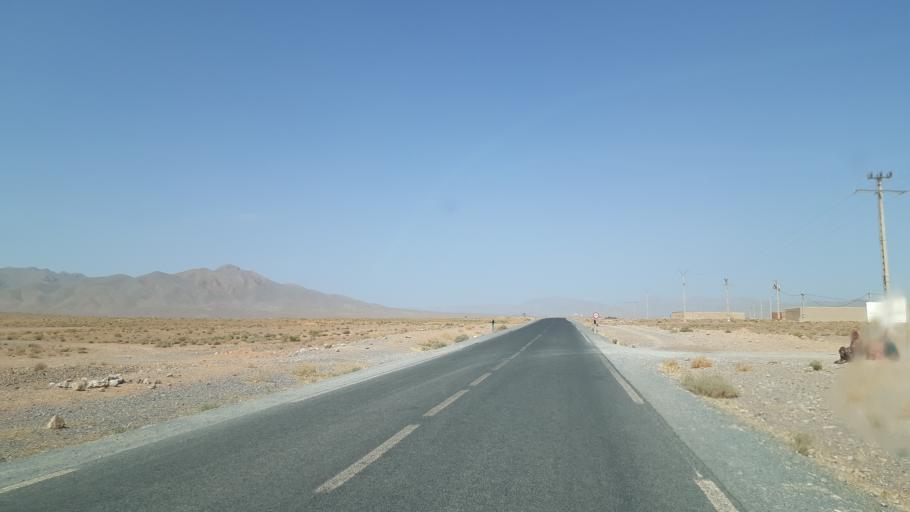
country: MA
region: Meknes-Tafilalet
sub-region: Errachidia
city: Amouguer
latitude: 32.2338
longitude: -4.6422
